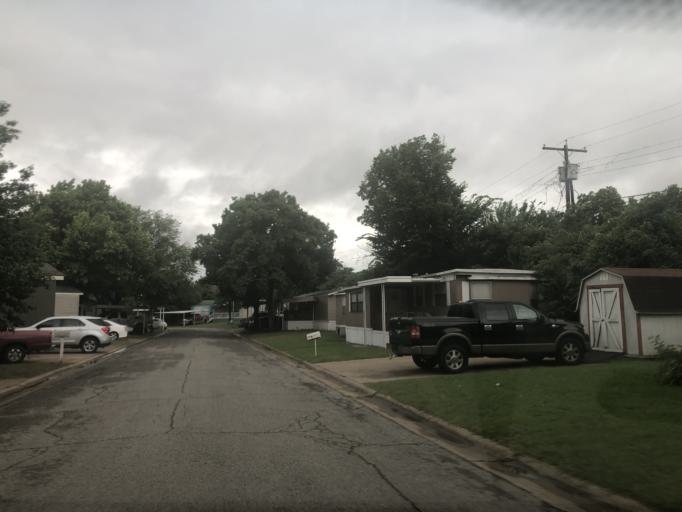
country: US
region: Texas
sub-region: Dallas County
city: Irving
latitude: 32.7932
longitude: -96.9582
